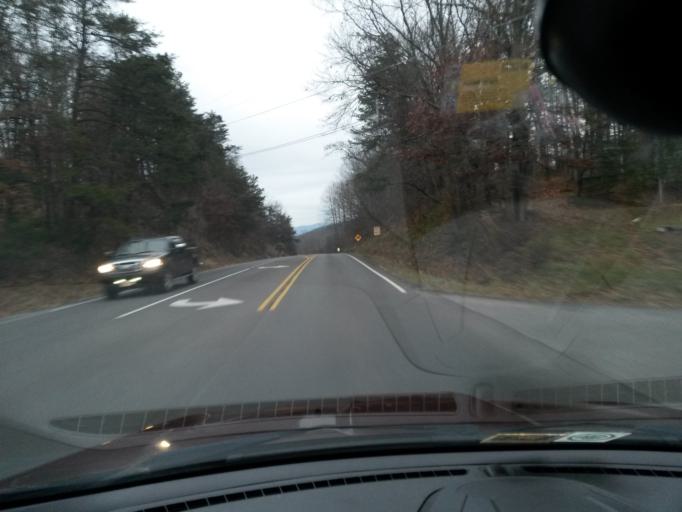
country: US
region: Virginia
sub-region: Alleghany County
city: Clifton Forge
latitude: 37.8176
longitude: -79.8038
